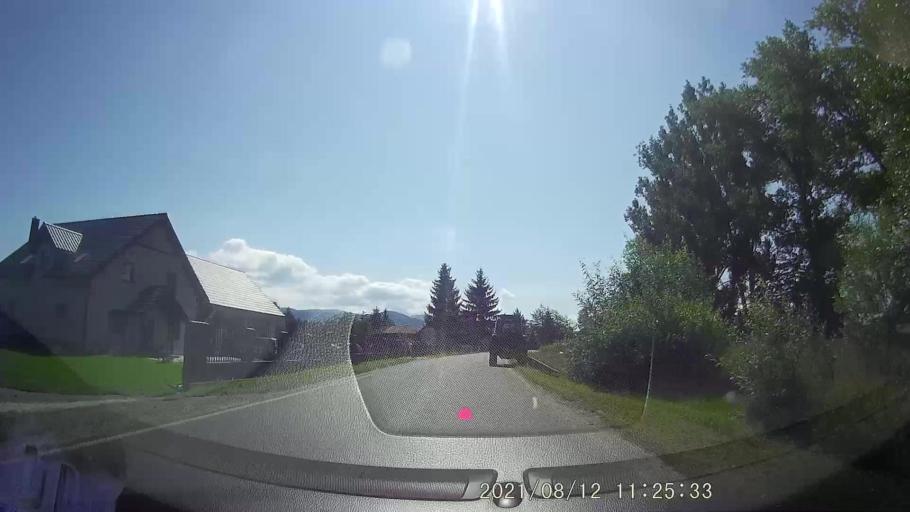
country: PL
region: Lower Silesian Voivodeship
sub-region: Powiat klodzki
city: Bystrzyca Klodzka
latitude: 50.2850
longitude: 16.6801
